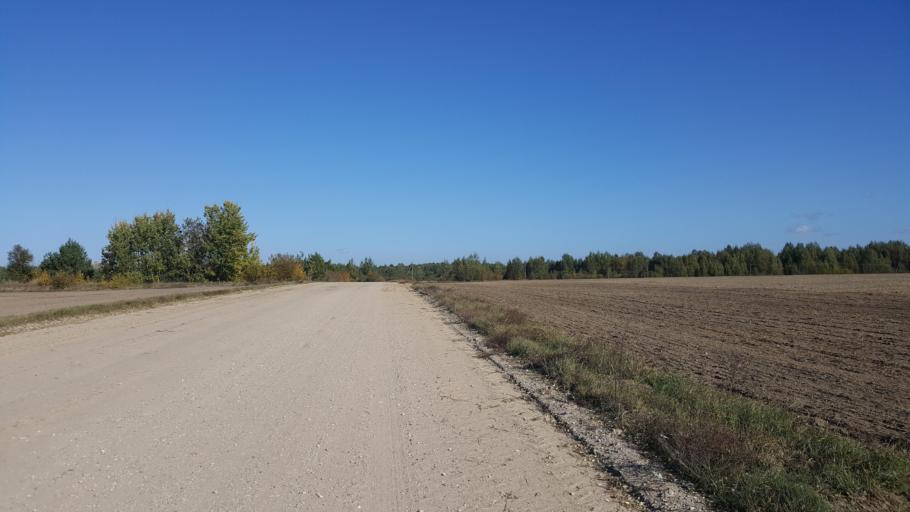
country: BY
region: Brest
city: Kamyanyets
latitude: 52.4323
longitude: 23.8842
